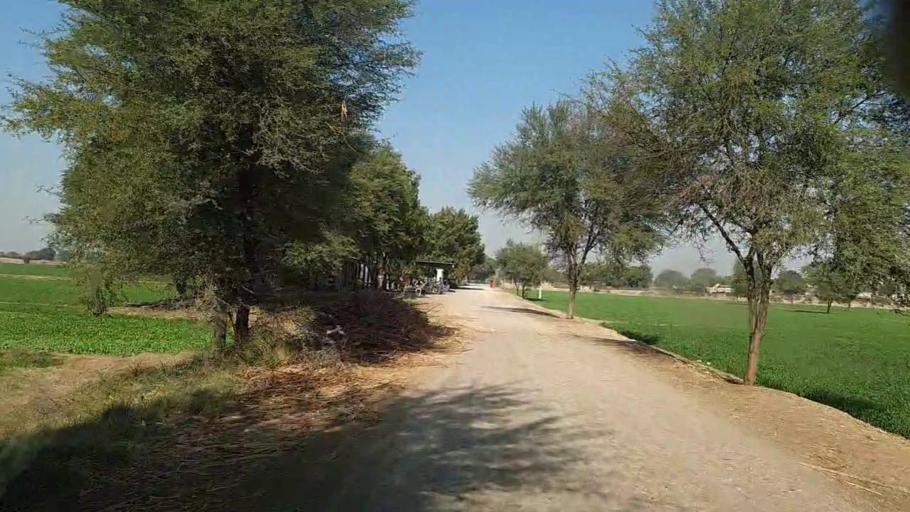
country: PK
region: Sindh
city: Khairpur
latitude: 28.0018
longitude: 69.8498
